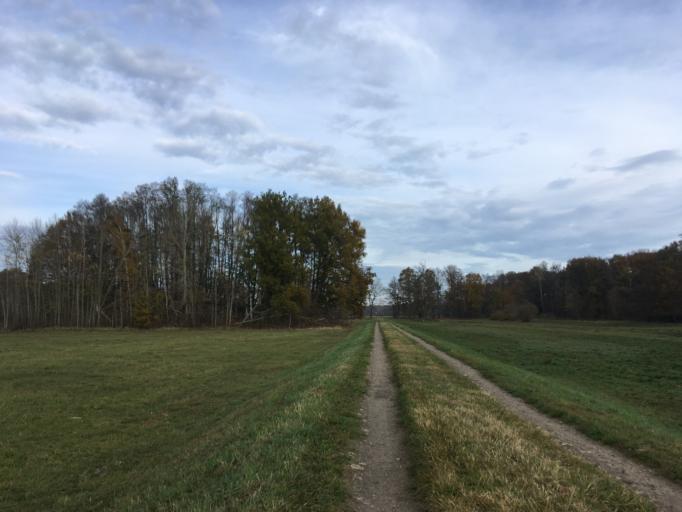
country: DE
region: Brandenburg
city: Schlepzig
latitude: 52.0322
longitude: 13.8546
